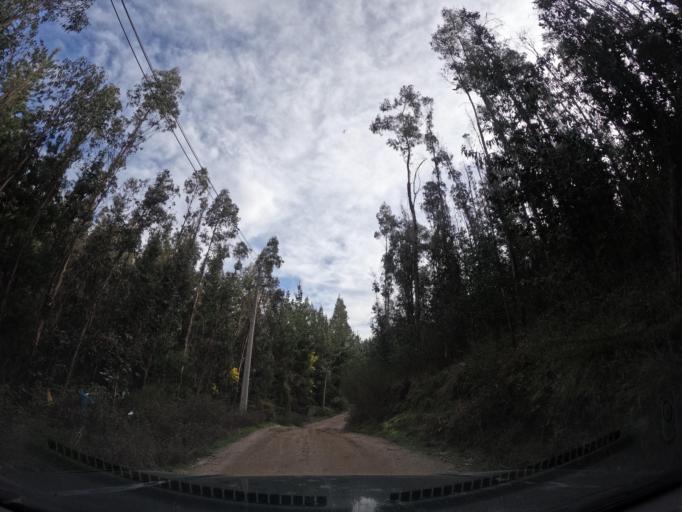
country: CL
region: Biobio
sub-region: Provincia de Concepcion
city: Chiguayante
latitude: -37.0165
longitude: -72.9105
